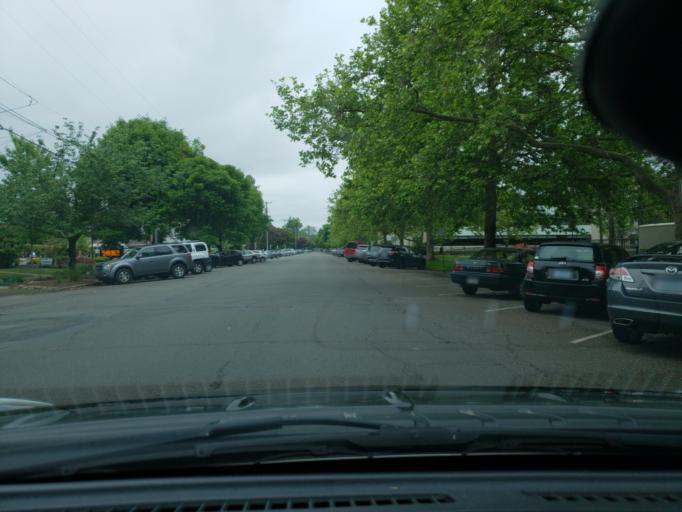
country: US
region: Oregon
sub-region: Marion County
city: Salem
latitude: 44.9441
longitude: -123.0294
